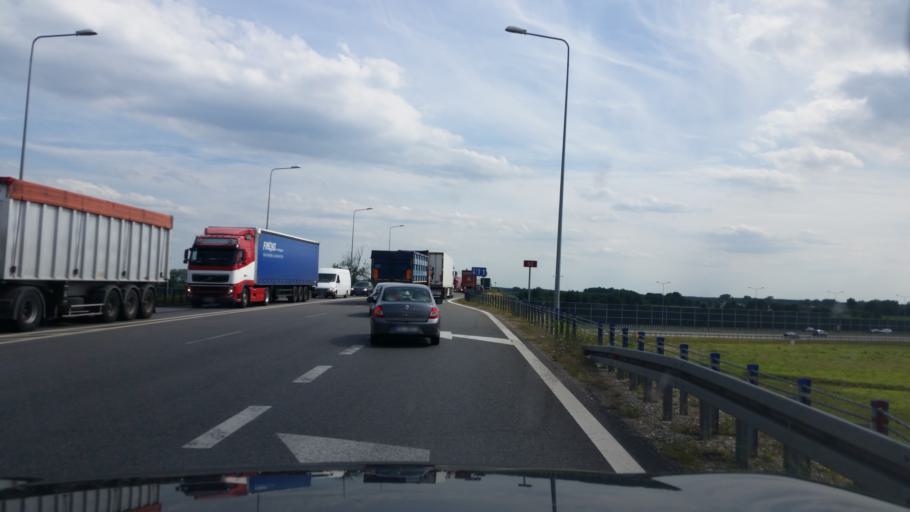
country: PL
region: Masovian Voivodeship
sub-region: Powiat zyrardowski
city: Wiskitki
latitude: 52.0908
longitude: 20.3638
